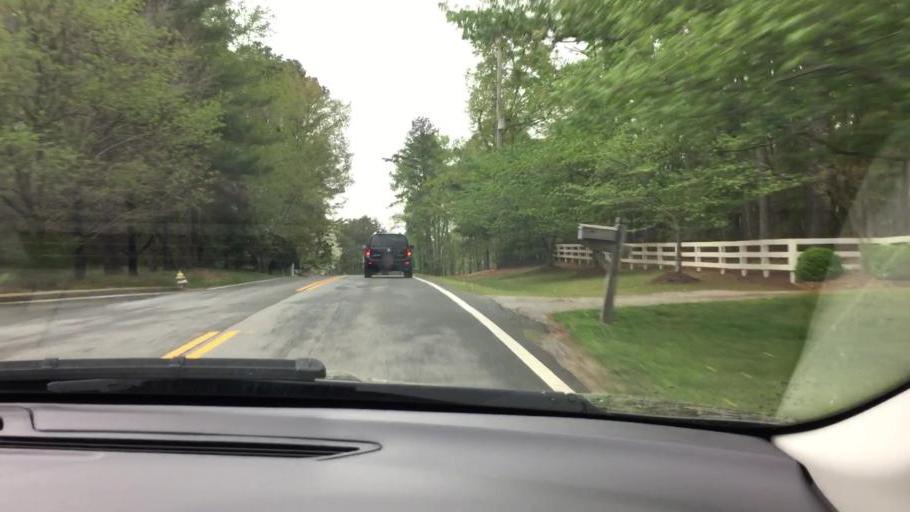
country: US
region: Georgia
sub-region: Fulton County
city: Milton
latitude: 34.1469
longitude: -84.2645
